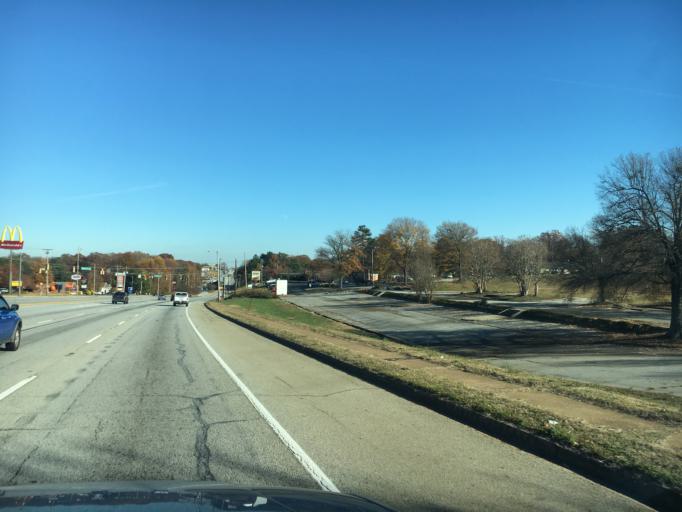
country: US
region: South Carolina
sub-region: Greenville County
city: Greer
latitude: 34.9487
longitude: -82.2368
